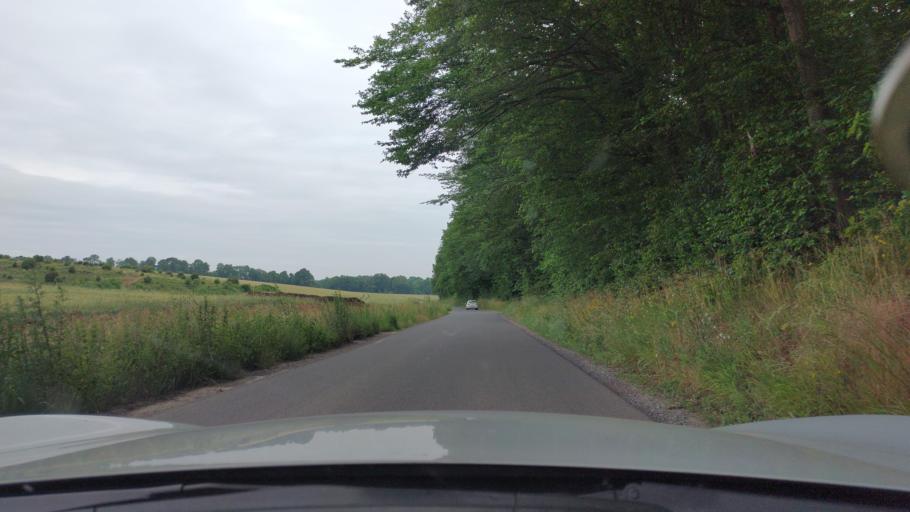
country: FR
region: Picardie
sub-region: Departement de l'Oise
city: Betz
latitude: 49.1450
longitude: 2.9631
